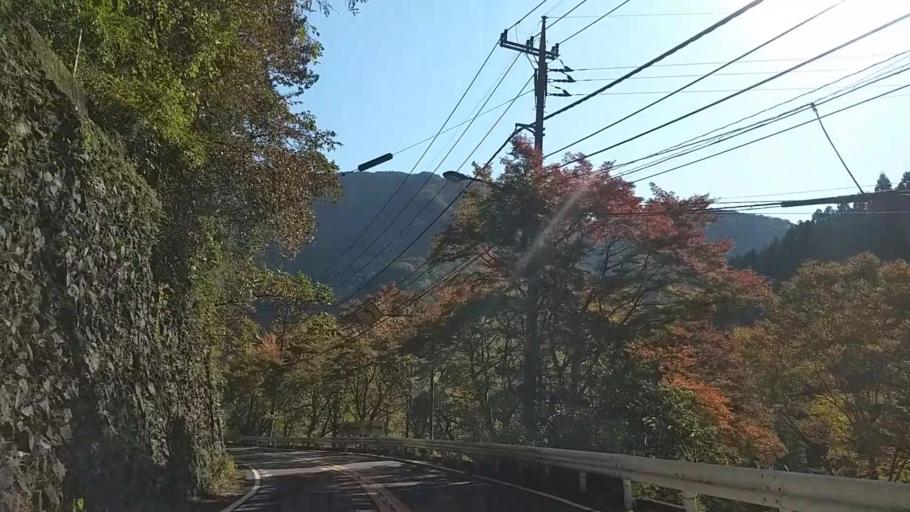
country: JP
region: Tokyo
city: Itsukaichi
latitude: 35.7939
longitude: 139.0578
